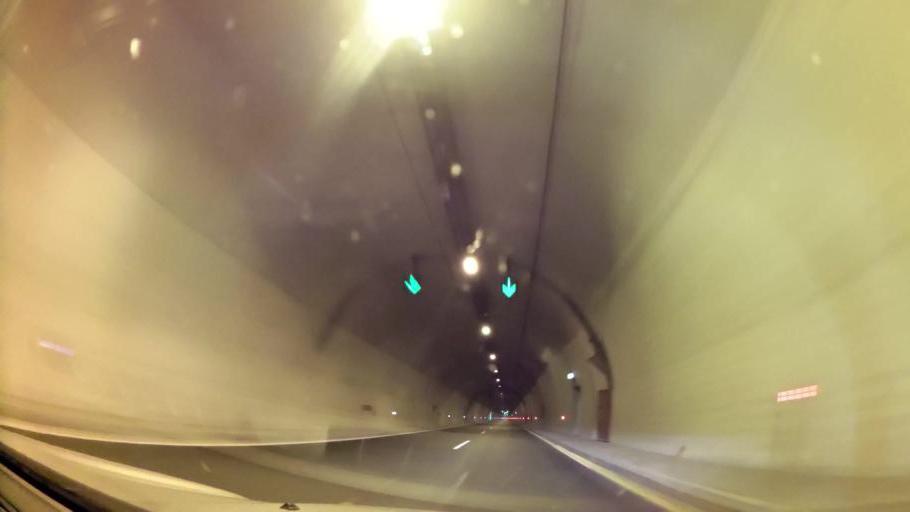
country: GR
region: Central Macedonia
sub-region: Nomos Imathias
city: Rizomata
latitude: 40.3835
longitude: 22.1255
